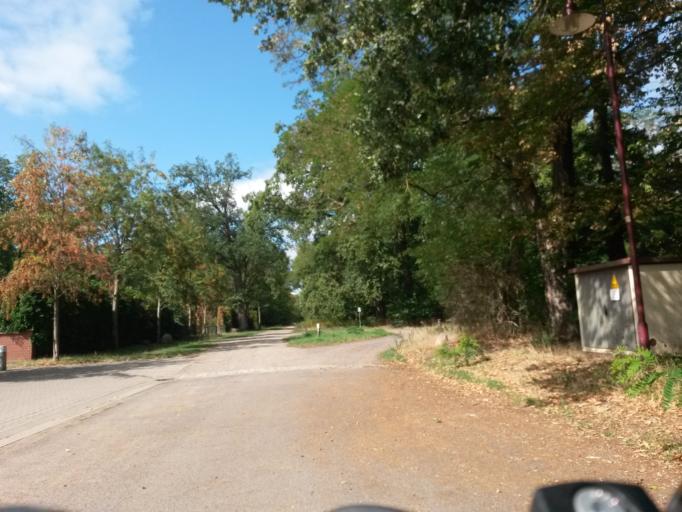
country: DE
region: Saxony-Anhalt
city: Jerichow
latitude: 52.4399
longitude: 11.9579
